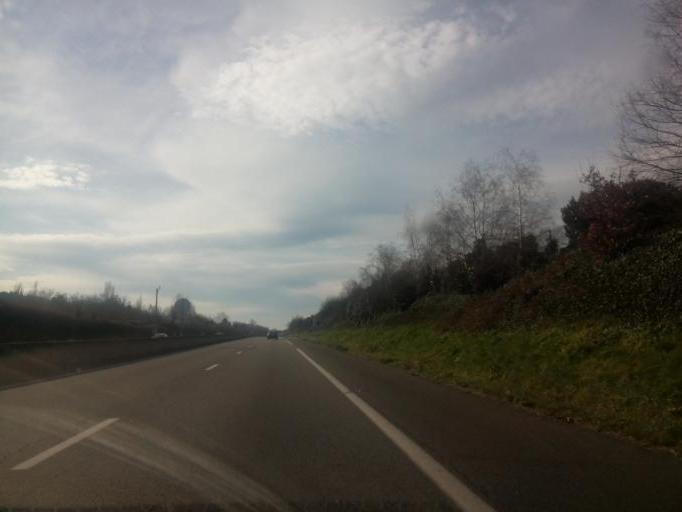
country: FR
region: Rhone-Alpes
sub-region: Departement du Rhone
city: Irigny
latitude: 45.6881
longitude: 4.8123
